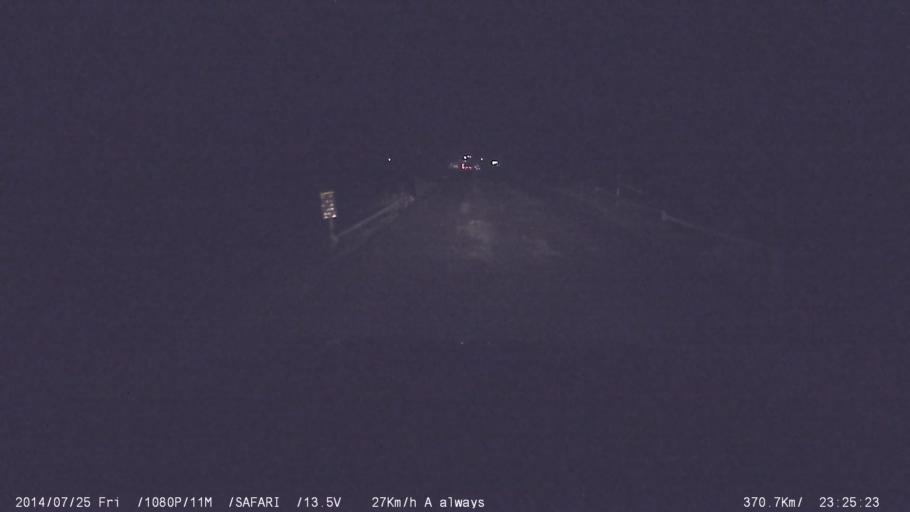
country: IN
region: Tamil Nadu
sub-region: Coimbatore
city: Madukkarai
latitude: 10.8692
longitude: 76.8852
